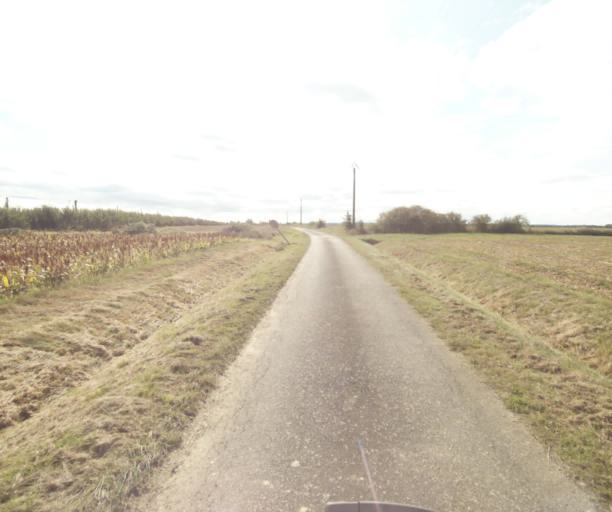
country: FR
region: Midi-Pyrenees
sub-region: Departement du Tarn-et-Garonne
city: Verdun-sur-Garonne
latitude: 43.8703
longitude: 1.1800
